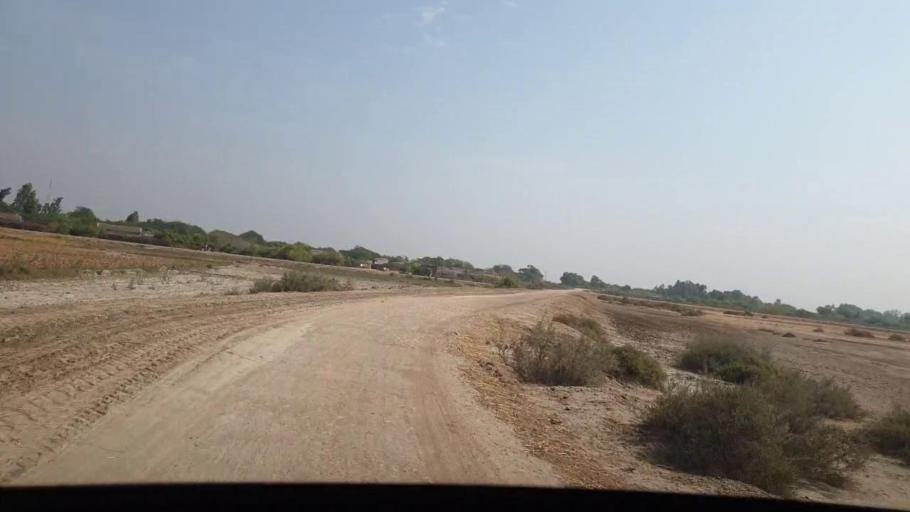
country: PK
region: Sindh
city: Chuhar Jamali
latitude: 24.2695
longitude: 67.9380
